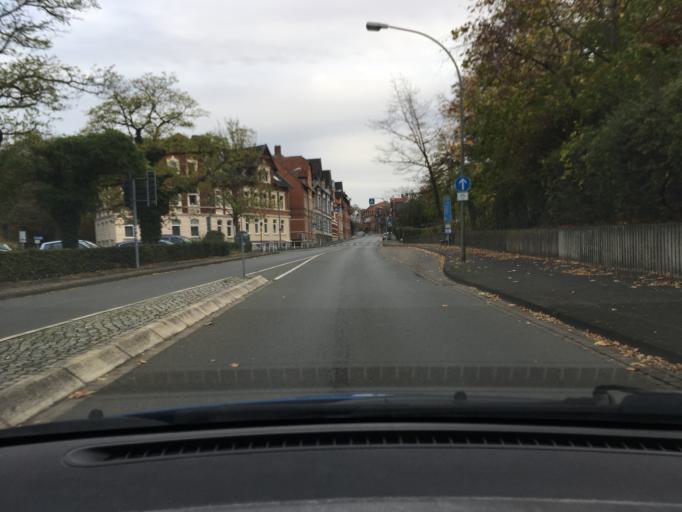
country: DE
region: Lower Saxony
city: Helmstedt
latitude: 52.2269
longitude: 11.0044
